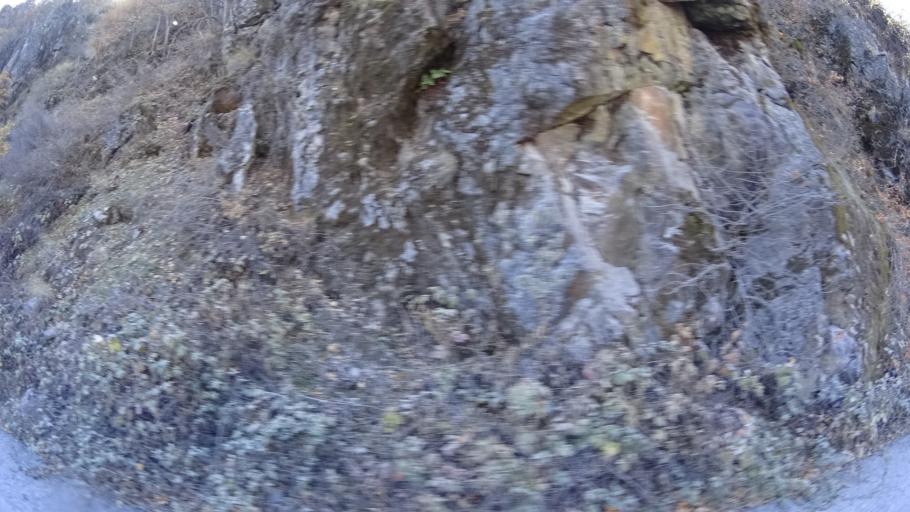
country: US
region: California
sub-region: Siskiyou County
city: Yreka
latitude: 41.8258
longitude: -122.6606
